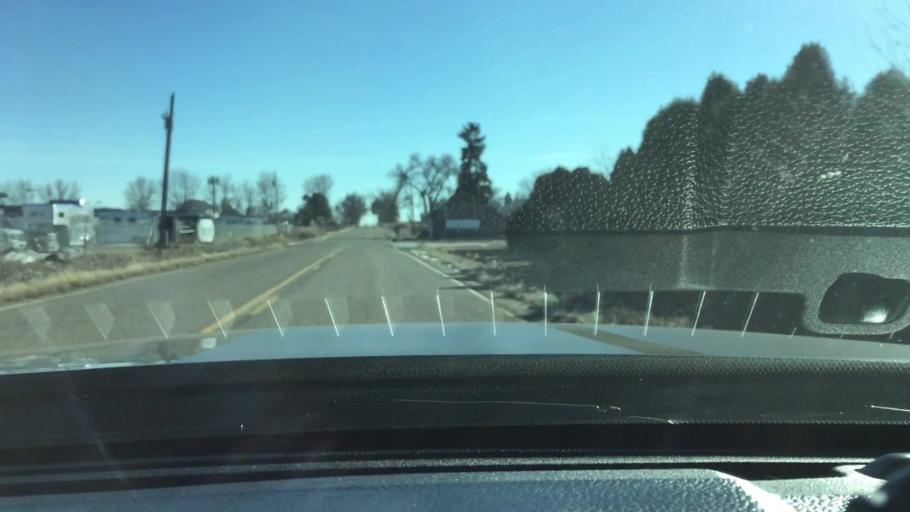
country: US
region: Colorado
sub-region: Weld County
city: Johnstown
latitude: 40.3560
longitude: -104.9835
